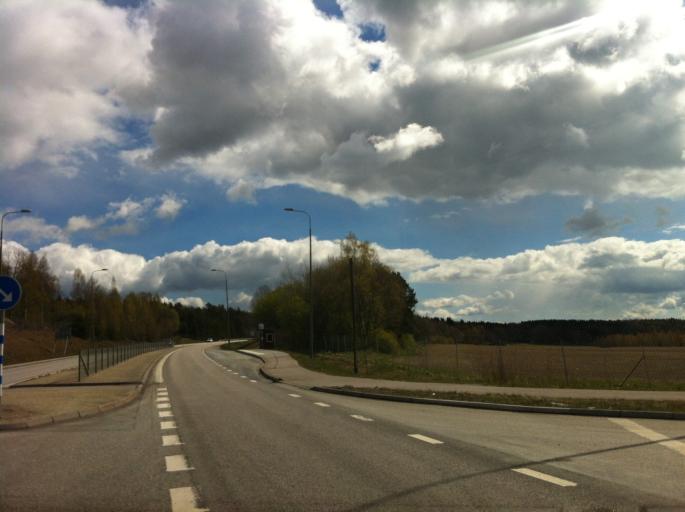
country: SE
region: Stockholm
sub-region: Osterakers Kommun
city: Akersberga
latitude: 59.5473
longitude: 18.2241
